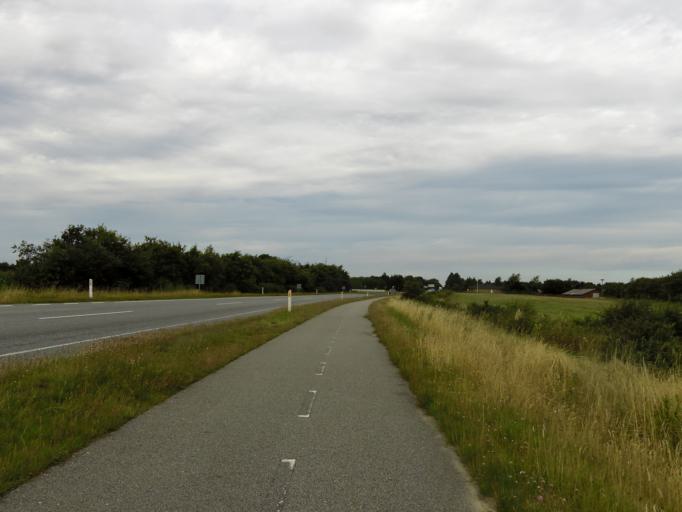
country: DK
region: South Denmark
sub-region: Esbjerg Kommune
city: Ribe
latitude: 55.3128
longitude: 8.7956
